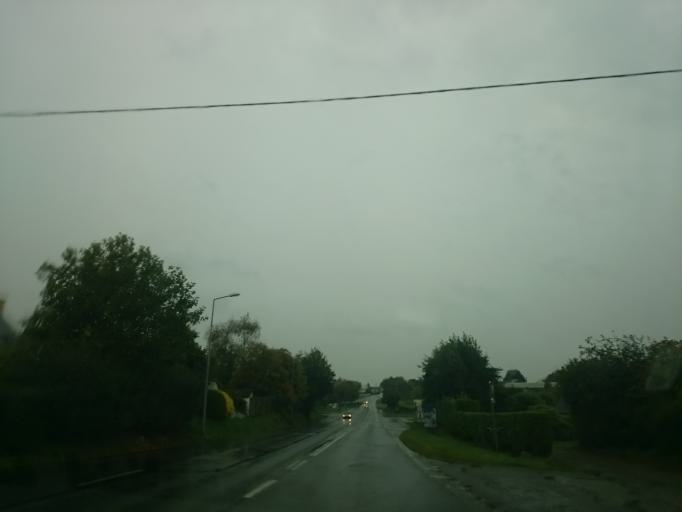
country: FR
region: Brittany
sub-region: Departement du Finistere
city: Plabennec
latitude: 48.5086
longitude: -4.4172
